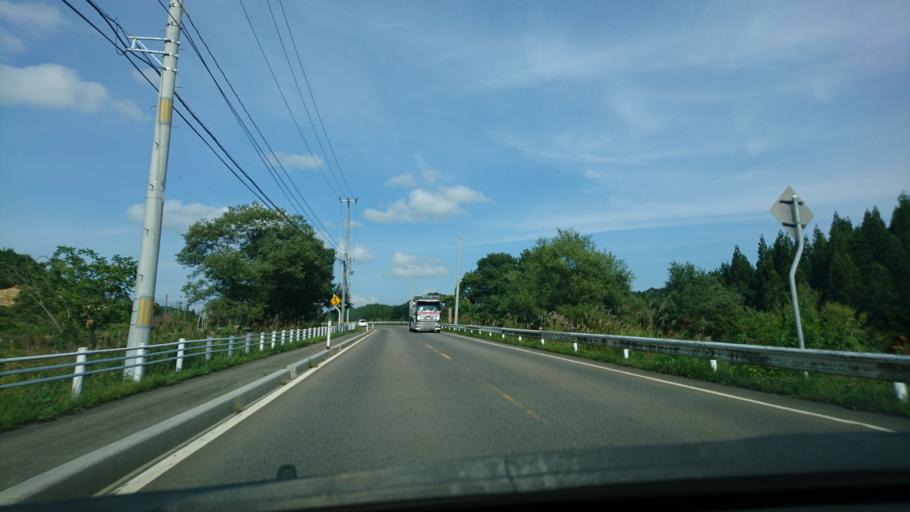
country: JP
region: Akita
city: Yokotemachi
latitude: 39.3007
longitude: 140.7374
